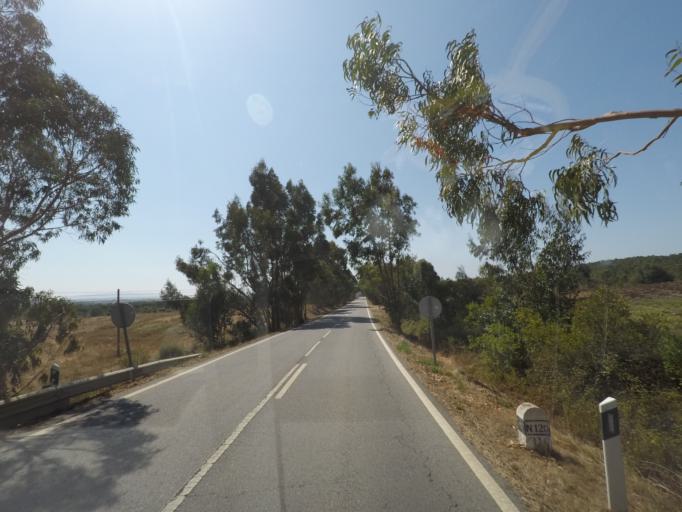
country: PT
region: Beja
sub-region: Odemira
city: Sao Teotonio
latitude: 37.5260
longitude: -8.6999
